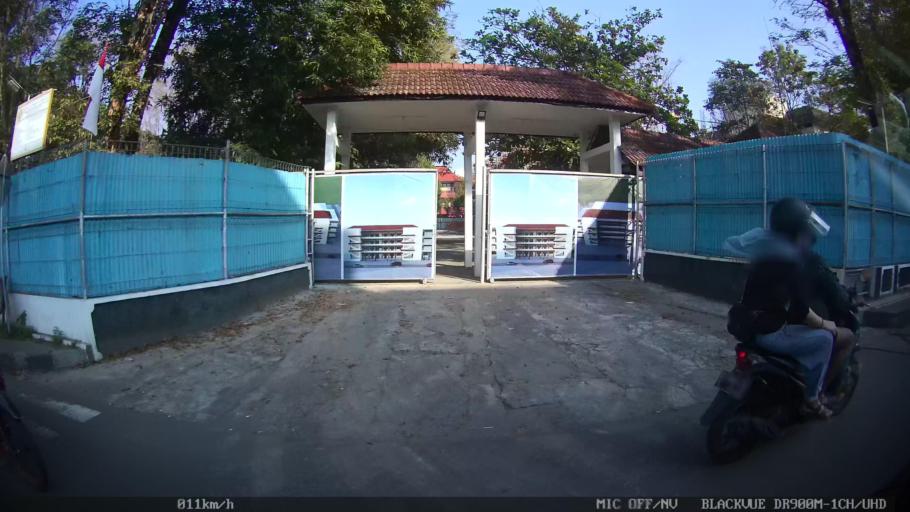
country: ID
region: Daerah Istimewa Yogyakarta
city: Depok
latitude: -7.7642
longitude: 110.4114
